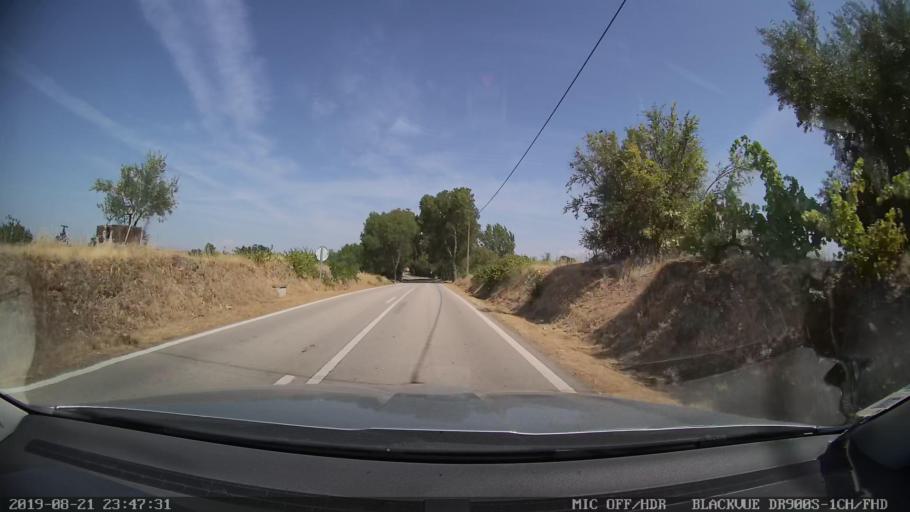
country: PT
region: Castelo Branco
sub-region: Idanha-A-Nova
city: Idanha-a-Nova
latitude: 39.8531
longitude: -7.2574
